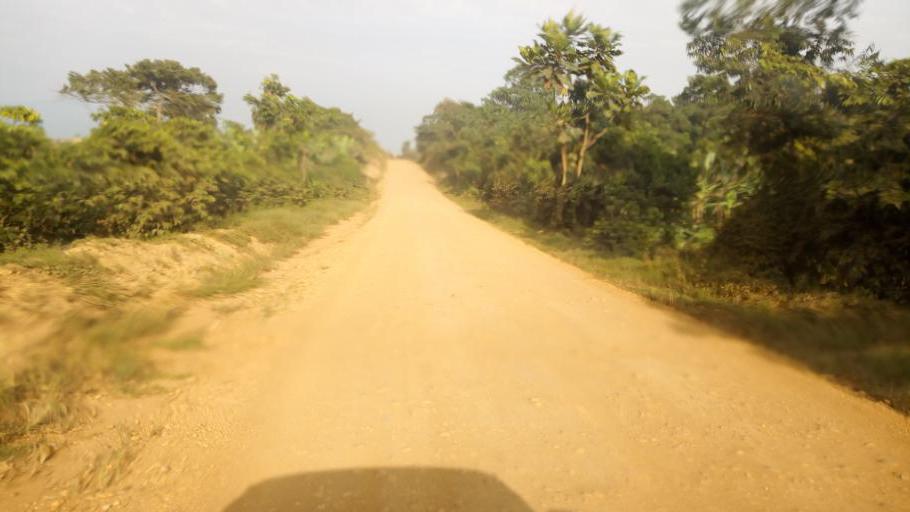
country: UG
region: Western Region
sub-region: Kanungu District
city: Ntungamo
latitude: -0.8348
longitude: 29.6760
